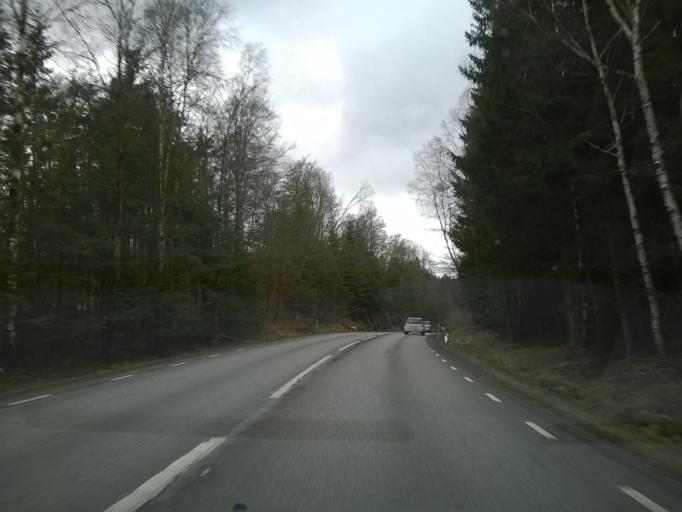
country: SE
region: Halland
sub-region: Varbergs Kommun
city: Tvaaker
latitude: 57.1481
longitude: 12.5993
